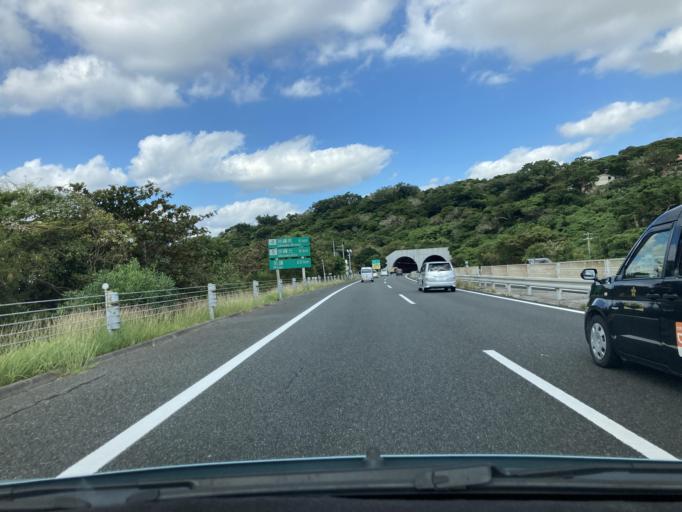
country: JP
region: Okinawa
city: Chatan
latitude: 26.3050
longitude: 127.7900
